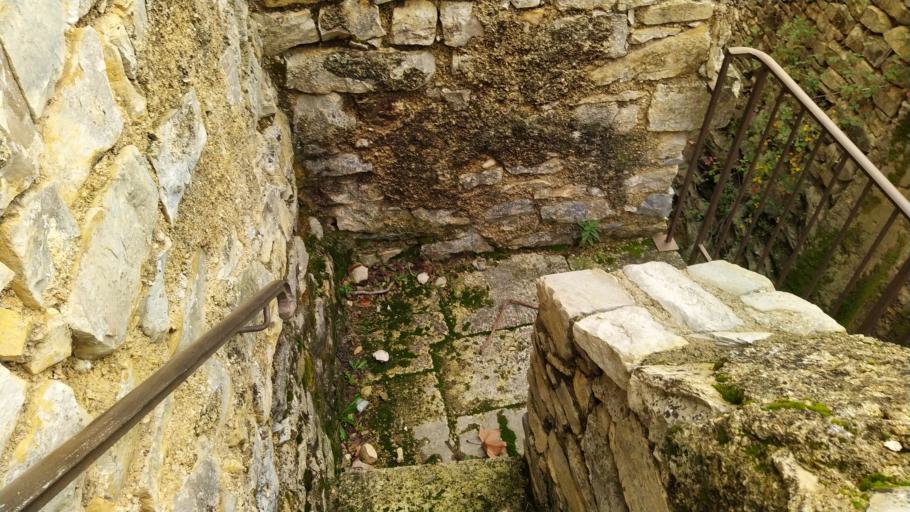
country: FR
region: Languedoc-Roussillon
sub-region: Departement du Gard
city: Poulx
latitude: 43.8720
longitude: 4.3997
